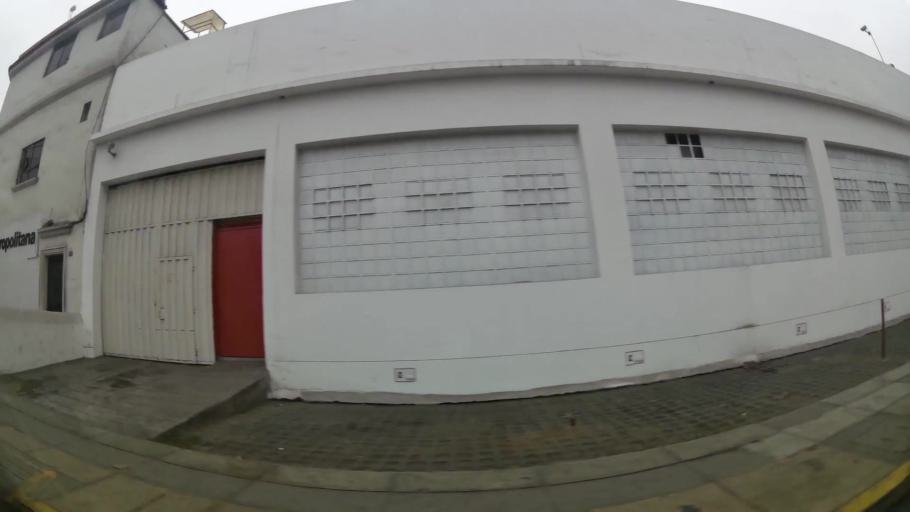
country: PE
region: Lima
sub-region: Lima
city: San Isidro
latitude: -12.0949
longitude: -77.0317
